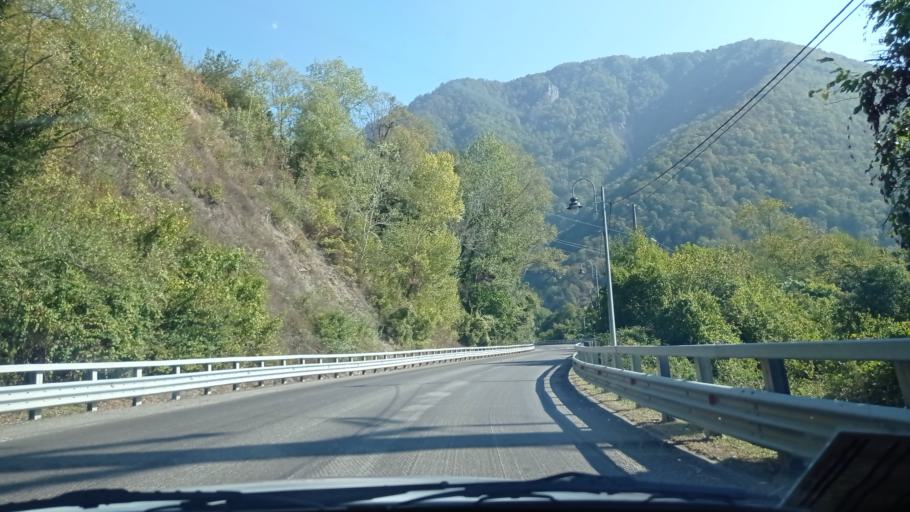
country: RU
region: Krasnodarskiy
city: Vysokoye
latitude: 43.5934
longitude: 40.0108
